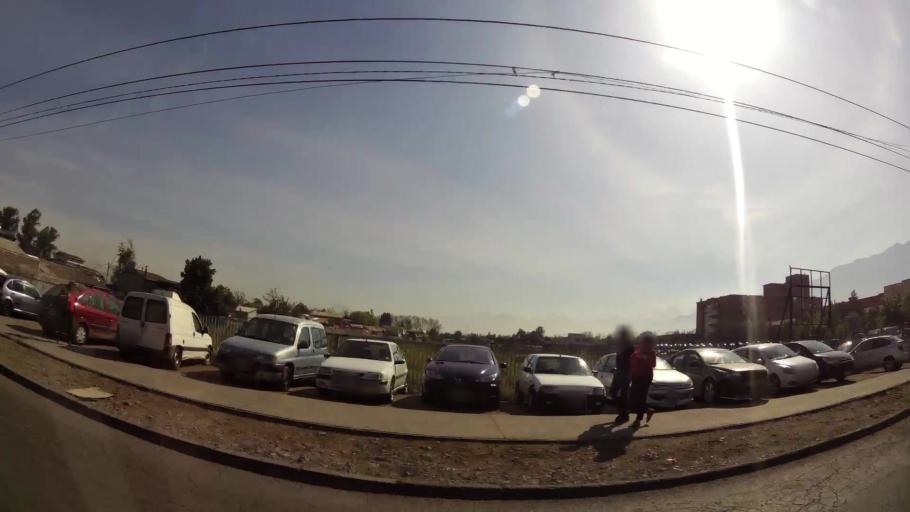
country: CL
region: Santiago Metropolitan
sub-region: Provincia de Santiago
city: Villa Presidente Frei, Nunoa, Santiago, Chile
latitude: -33.5013
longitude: -70.5811
